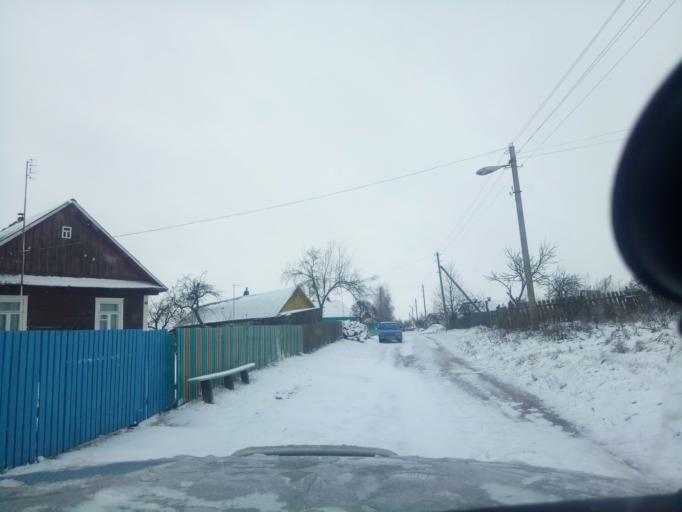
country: BY
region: Minsk
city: Klyetsk
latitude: 53.0220
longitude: 26.7123
